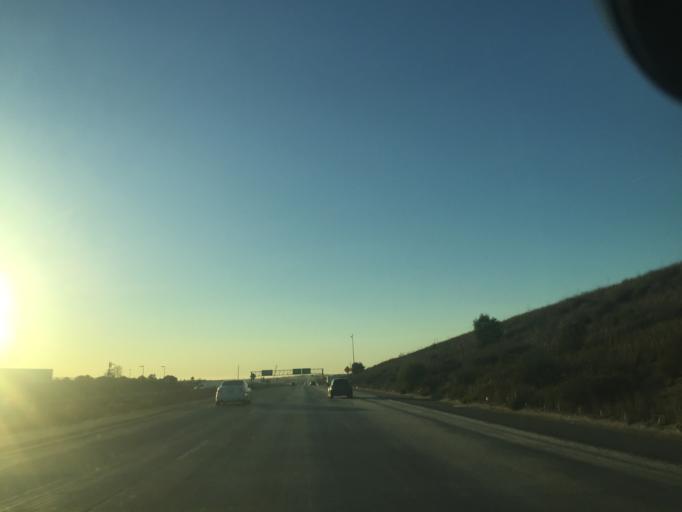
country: MX
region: Baja California
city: Tijuana
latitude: 32.5641
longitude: -116.9326
